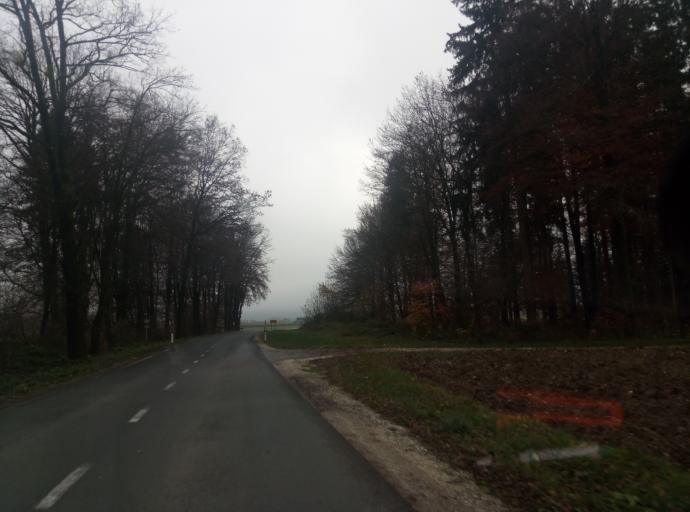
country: SI
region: Vodice
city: Vodice
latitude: 46.1798
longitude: 14.4896
